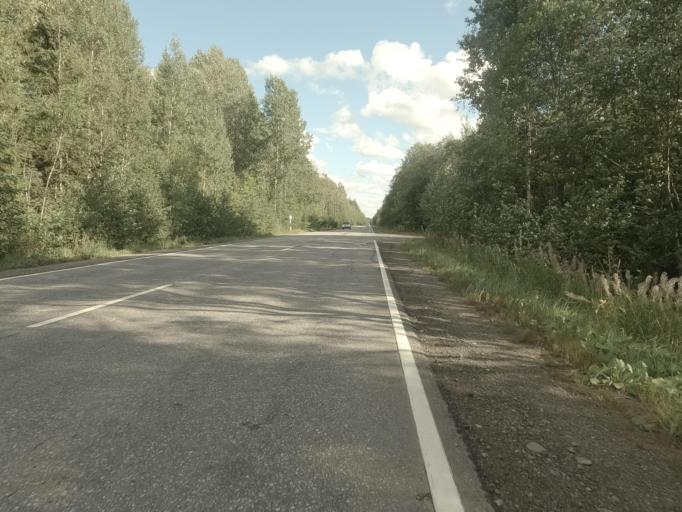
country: RU
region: Leningrad
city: Shcheglovo
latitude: 59.9970
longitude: 30.8754
